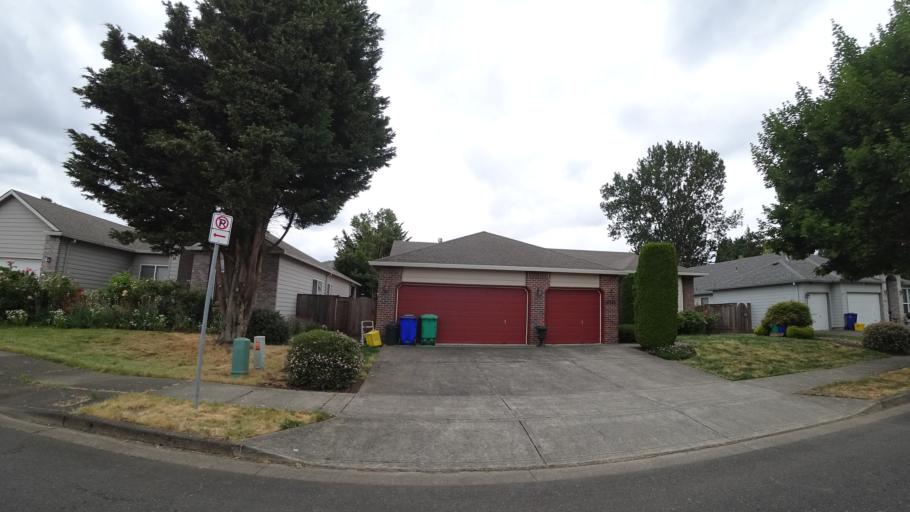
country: US
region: Washington
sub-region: Clark County
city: Vancouver
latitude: 45.5911
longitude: -122.6491
